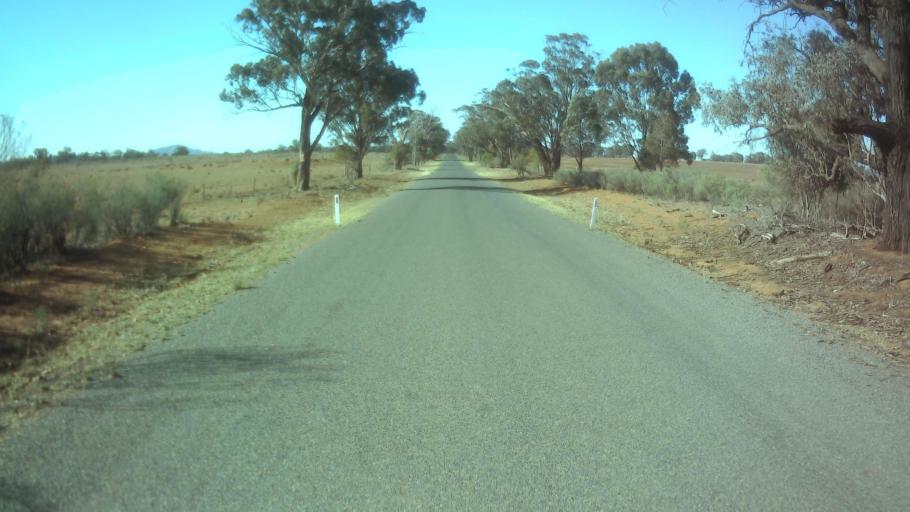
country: AU
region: New South Wales
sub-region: Forbes
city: Forbes
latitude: -33.7023
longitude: 147.8063
